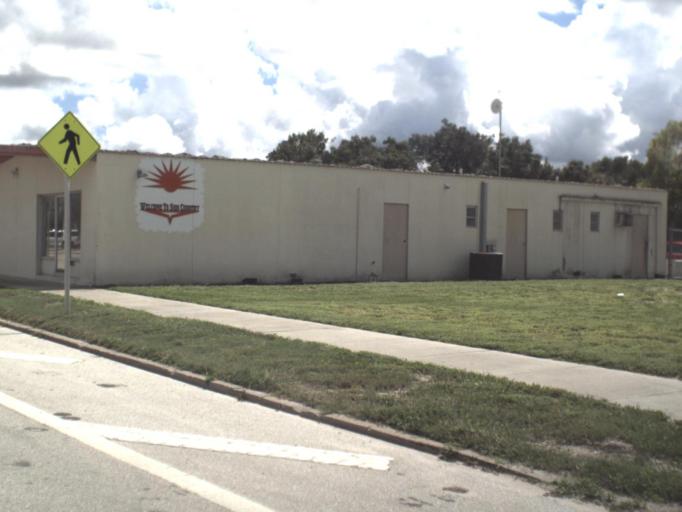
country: US
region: Florida
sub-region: DeSoto County
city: Arcadia
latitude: 27.2150
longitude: -81.8625
